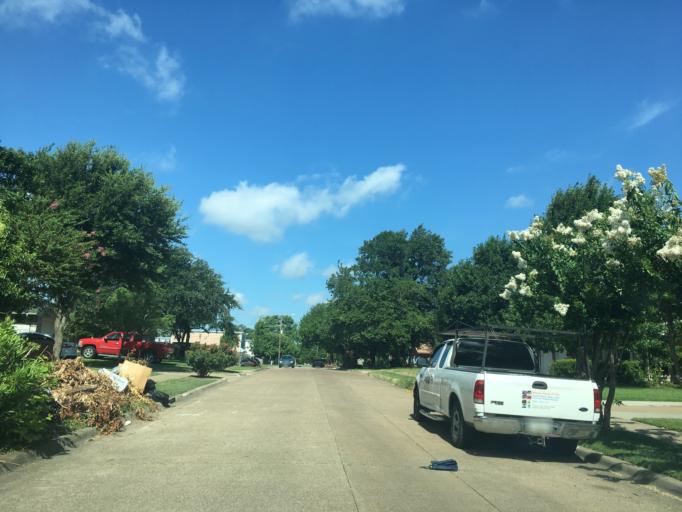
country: US
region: Texas
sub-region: Dallas County
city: Garland
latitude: 32.8455
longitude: -96.6636
